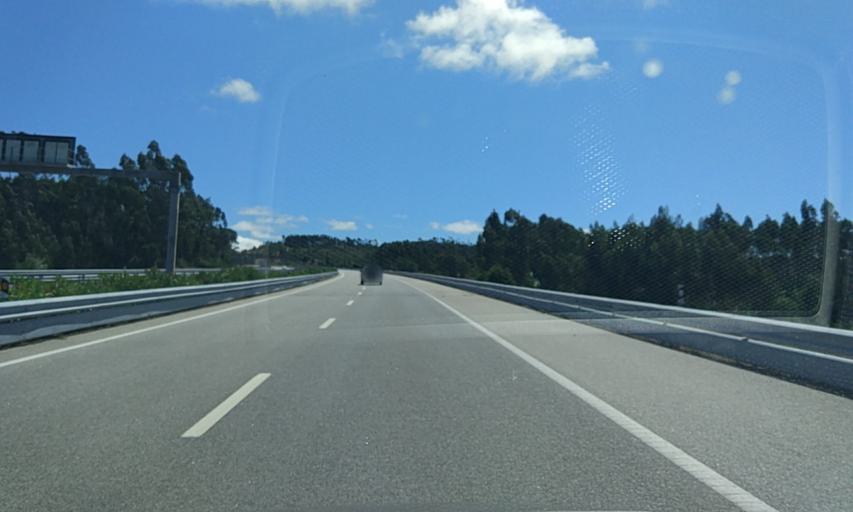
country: PT
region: Coimbra
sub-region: Figueira da Foz
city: Alhadas
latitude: 40.2030
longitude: -8.8103
